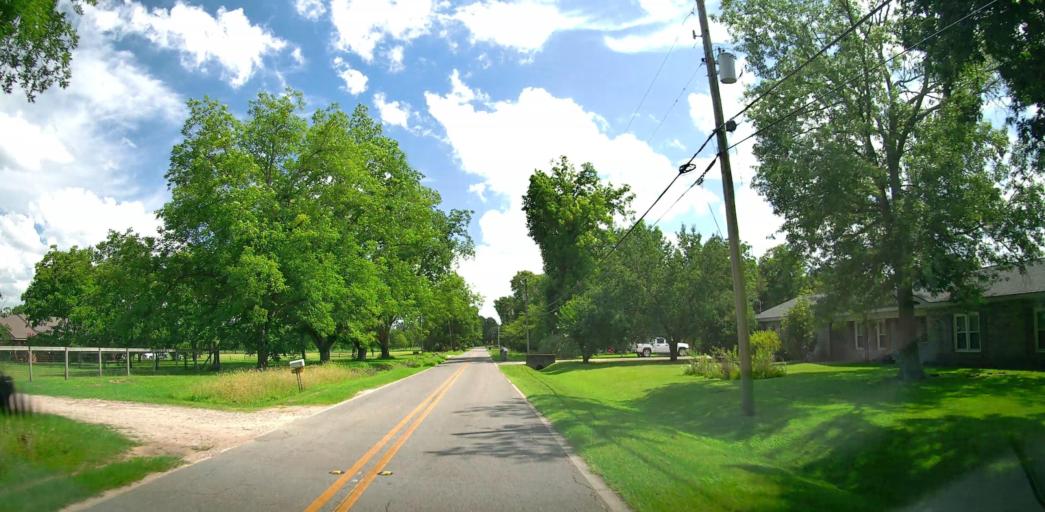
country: US
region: Georgia
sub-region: Houston County
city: Centerville
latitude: 32.7073
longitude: -83.6792
